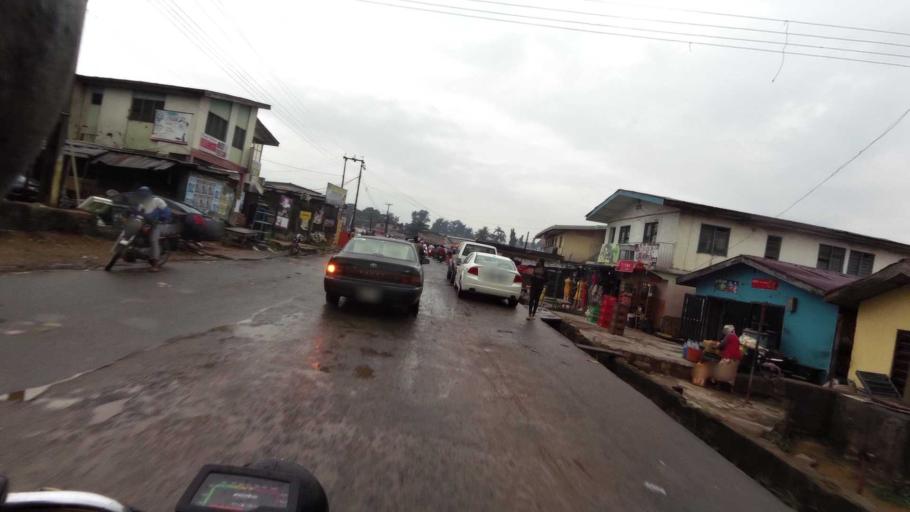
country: NG
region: Oyo
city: Ibadan
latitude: 7.4158
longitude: 3.9337
